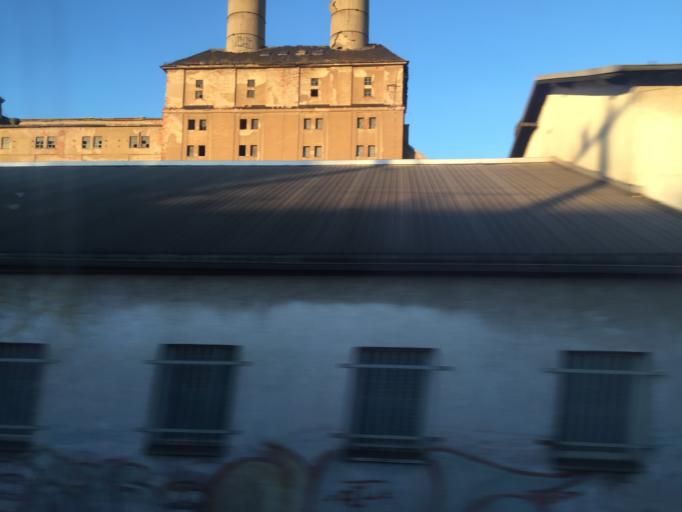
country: DE
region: Saxony
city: Heidenau
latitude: 51.0028
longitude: 13.8233
